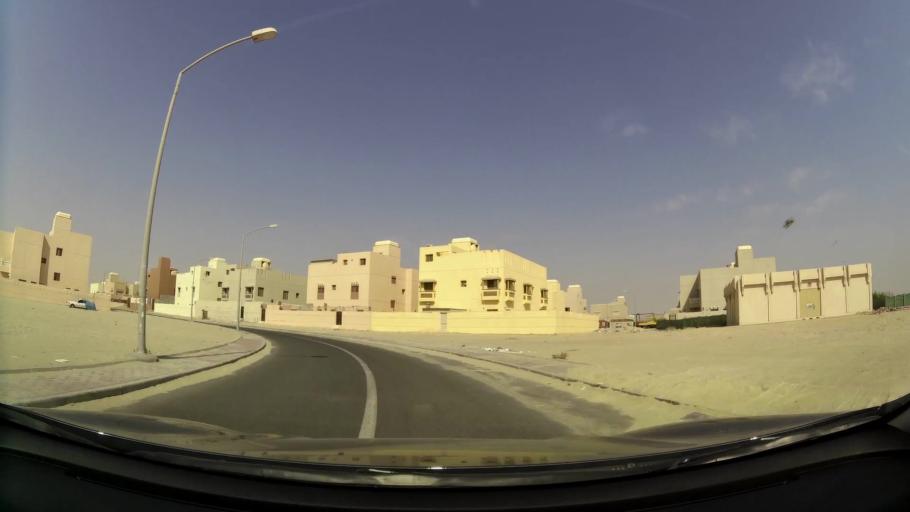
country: KW
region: Al Ahmadi
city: Al Wafrah
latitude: 28.8093
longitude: 48.0612
